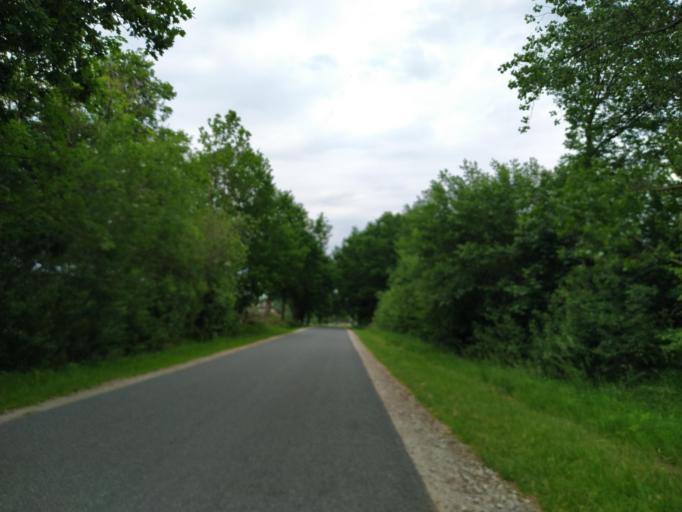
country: DE
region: Schleswig-Holstein
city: Gross Sarau
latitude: 53.7808
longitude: 10.7256
